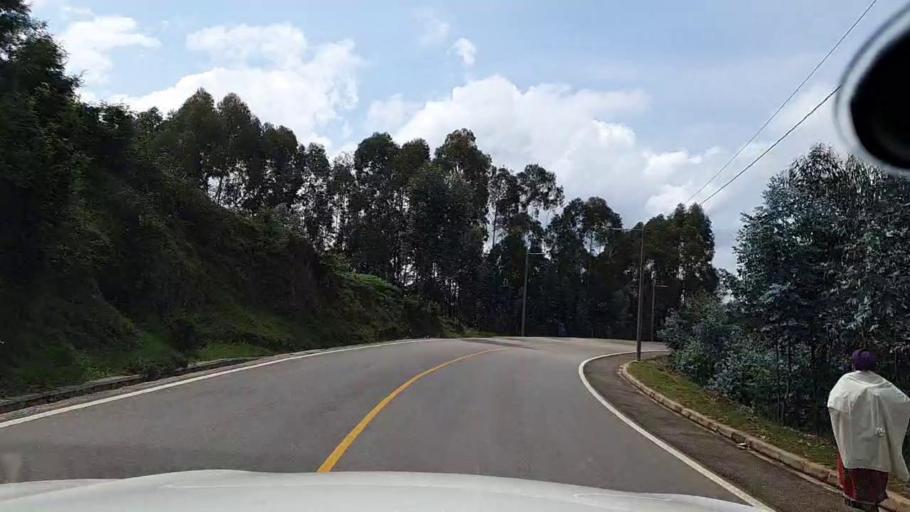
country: RW
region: Southern Province
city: Nzega
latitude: -2.5273
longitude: 29.4513
